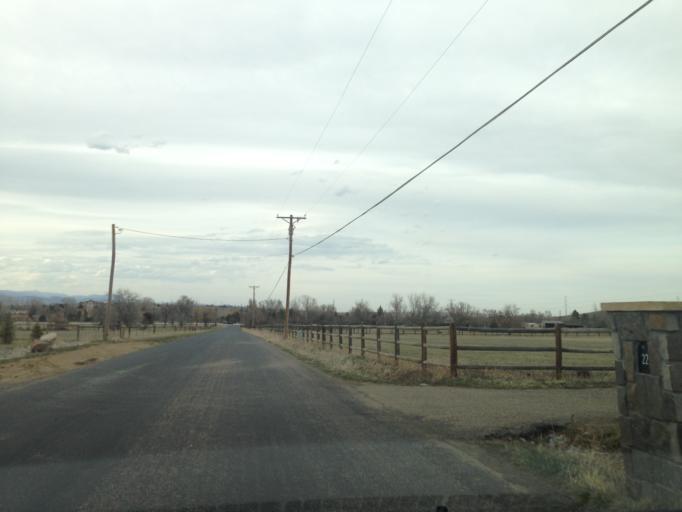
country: US
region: Colorado
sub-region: Boulder County
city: Superior
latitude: 39.9826
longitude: -105.1940
